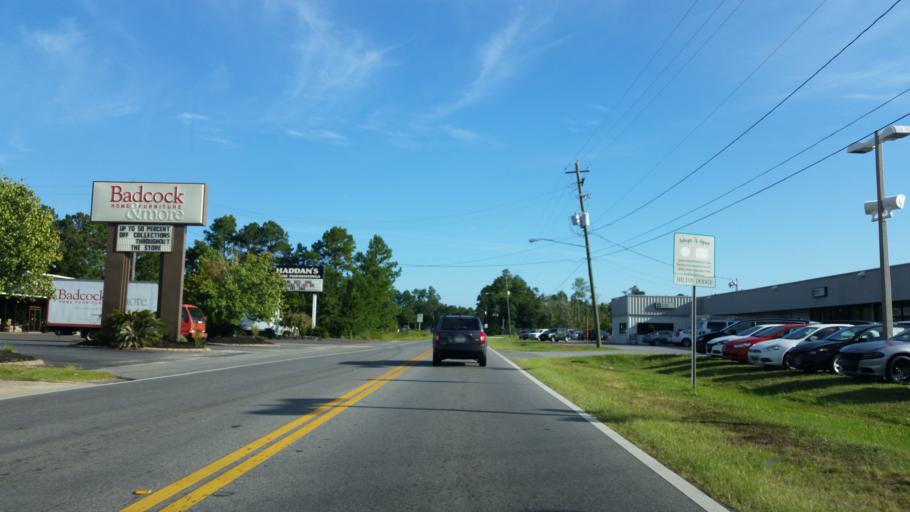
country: US
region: Florida
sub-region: Santa Rosa County
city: Milton
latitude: 30.6095
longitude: -87.0592
